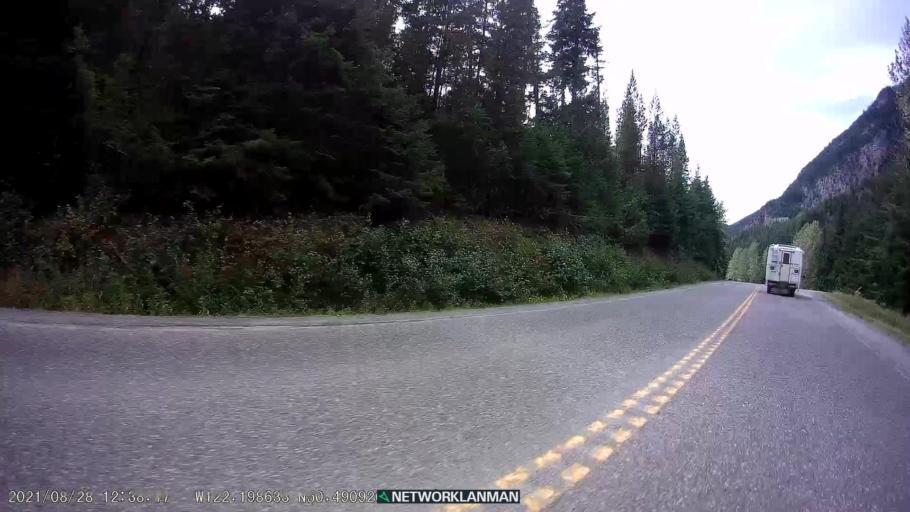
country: CA
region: British Columbia
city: Lillooet
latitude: 50.4915
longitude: -122.2042
